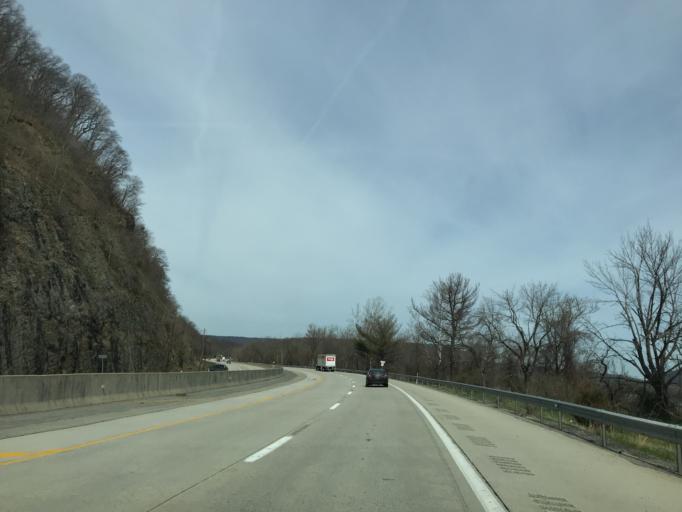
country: US
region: Pennsylvania
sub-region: Dauphin County
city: Millersburg
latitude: 40.4902
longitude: -76.9536
